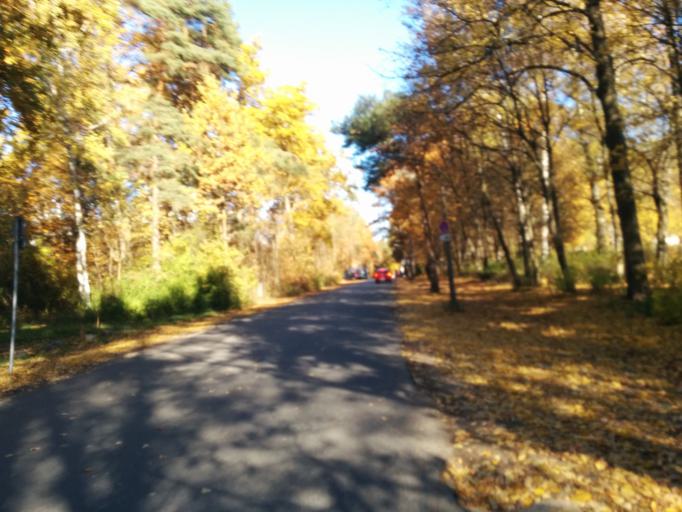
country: DE
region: Bavaria
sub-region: Regierungsbezirk Mittelfranken
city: Heroldsberg
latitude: 49.4811
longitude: 11.1335
